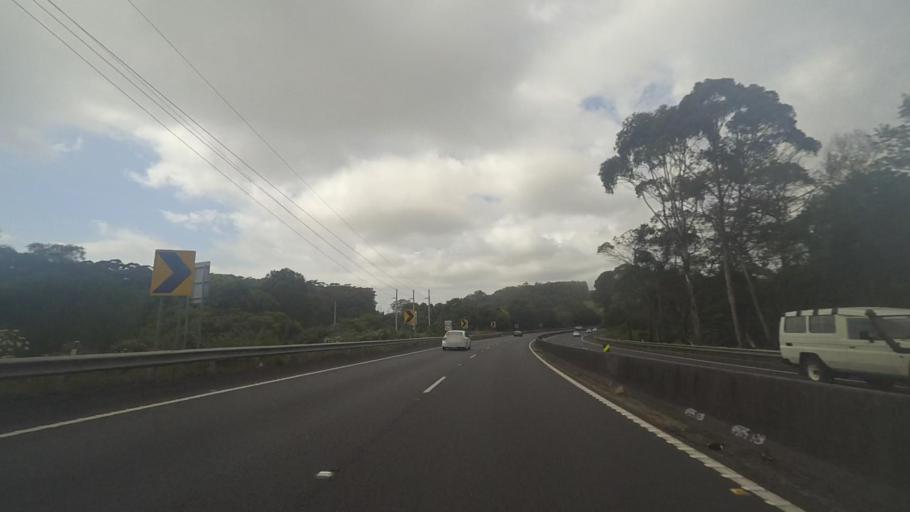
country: AU
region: New South Wales
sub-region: Wollongong
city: Bulli
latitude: -34.3358
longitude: 150.8805
